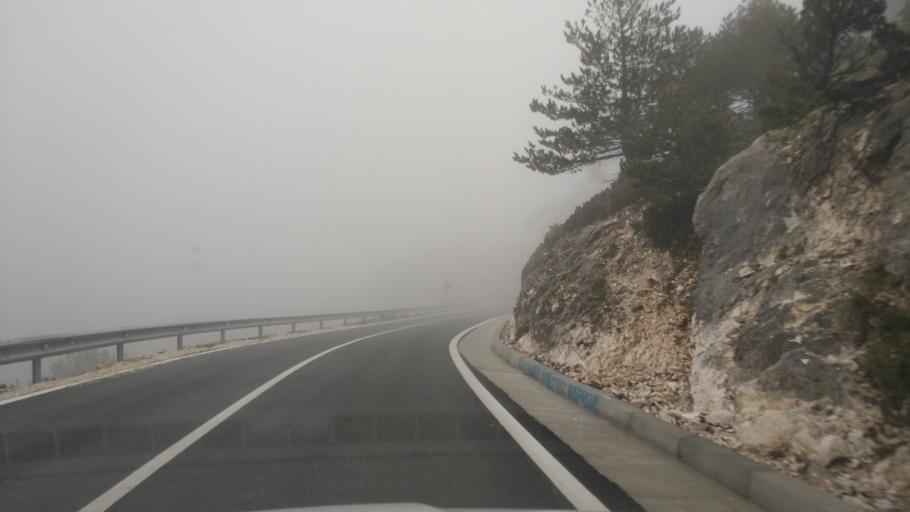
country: AL
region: Vlore
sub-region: Rrethi i Vlores
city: Vranisht
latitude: 40.1903
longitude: 19.5986
